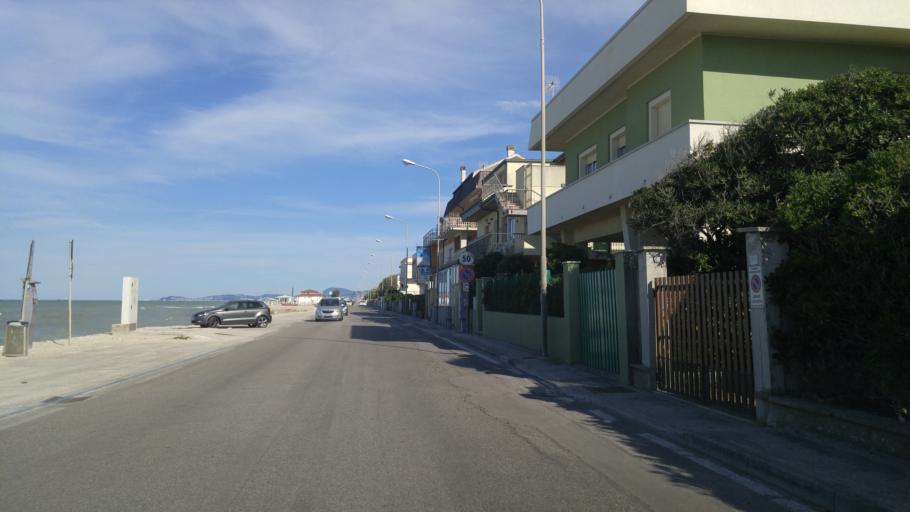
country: IT
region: The Marches
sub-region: Provincia di Ancona
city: Marina di Montemarciano
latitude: 43.6643
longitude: 13.3159
